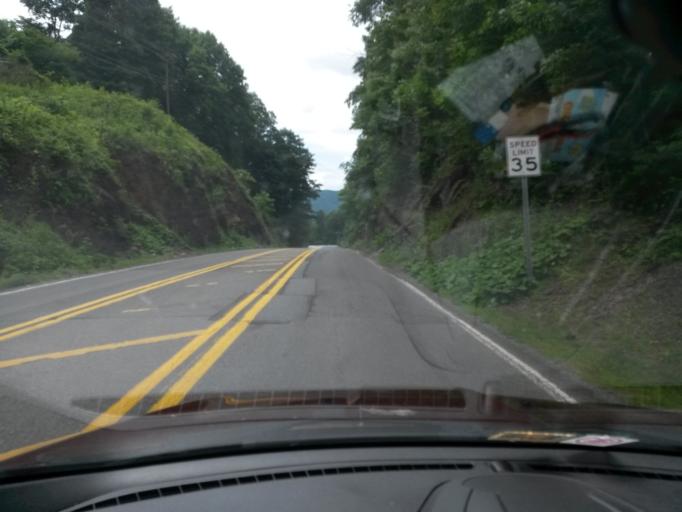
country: US
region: West Virginia
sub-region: Mercer County
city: Brush Fork
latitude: 37.2697
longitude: -81.2441
